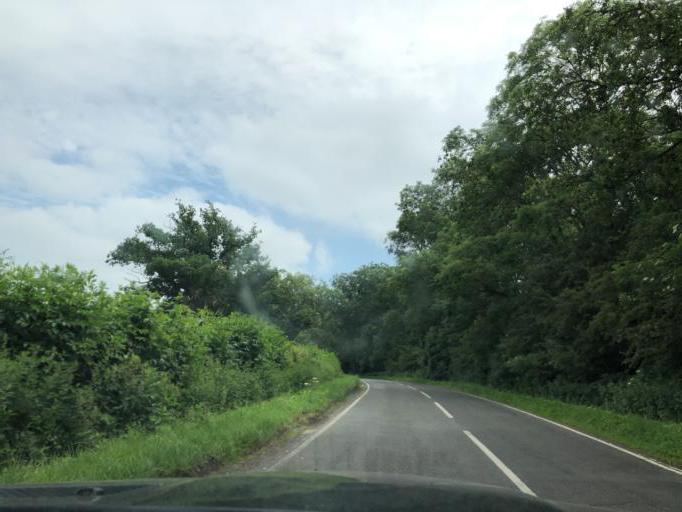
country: GB
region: England
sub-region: Warwickshire
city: Kenilworth
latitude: 52.3276
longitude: -1.6103
